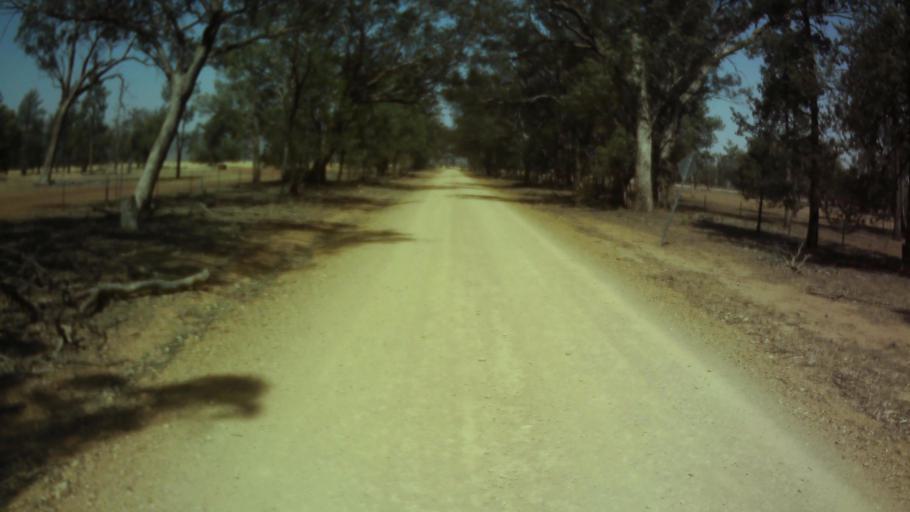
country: AU
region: New South Wales
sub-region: Weddin
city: Grenfell
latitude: -33.9957
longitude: 147.9206
